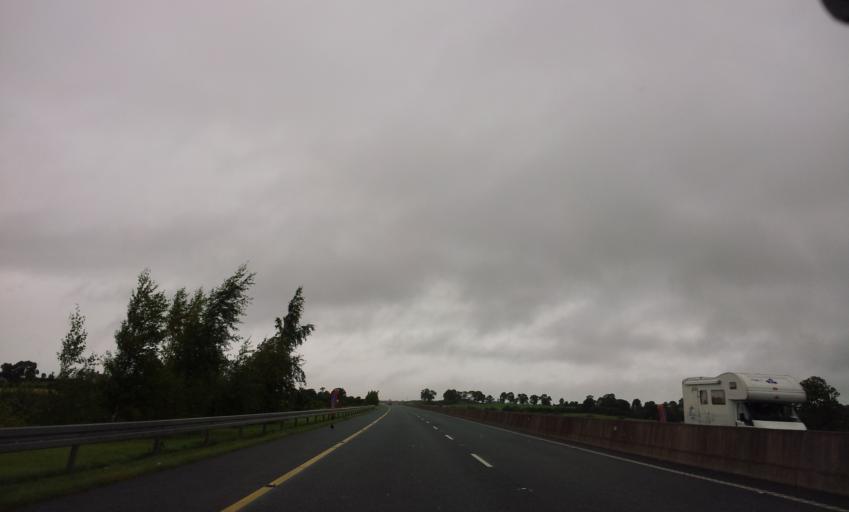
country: IE
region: Munster
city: Cahir
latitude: 52.4399
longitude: -7.9112
